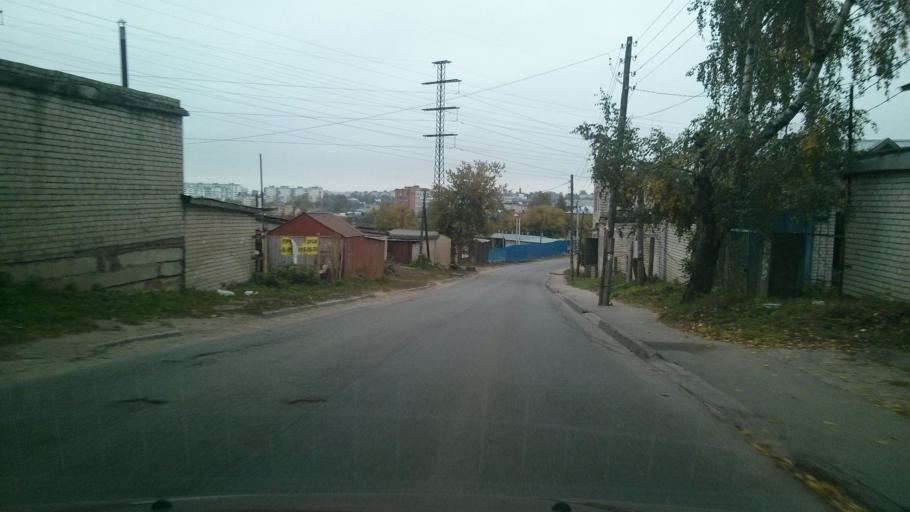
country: RU
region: Nizjnij Novgorod
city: Nizhniy Novgorod
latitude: 56.3087
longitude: 44.0093
